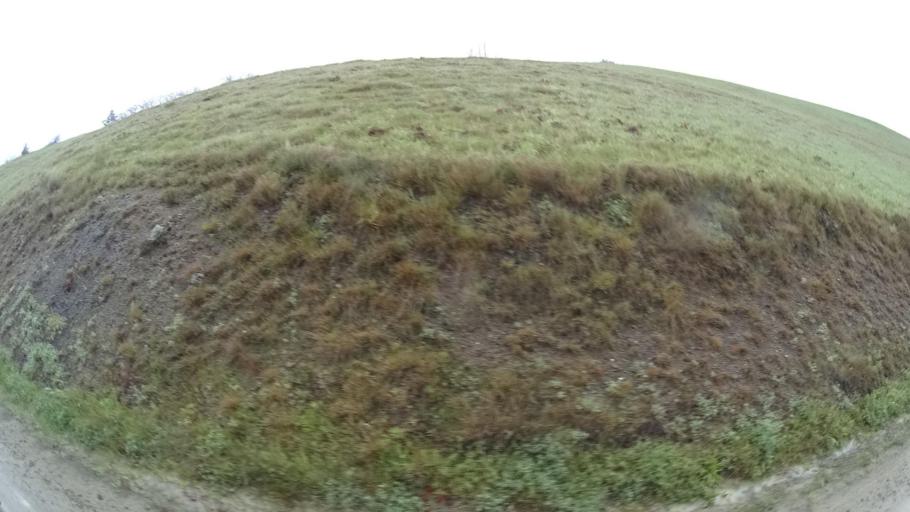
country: US
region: California
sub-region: Humboldt County
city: Westhaven-Moonstone
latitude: 41.1470
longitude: -123.8721
